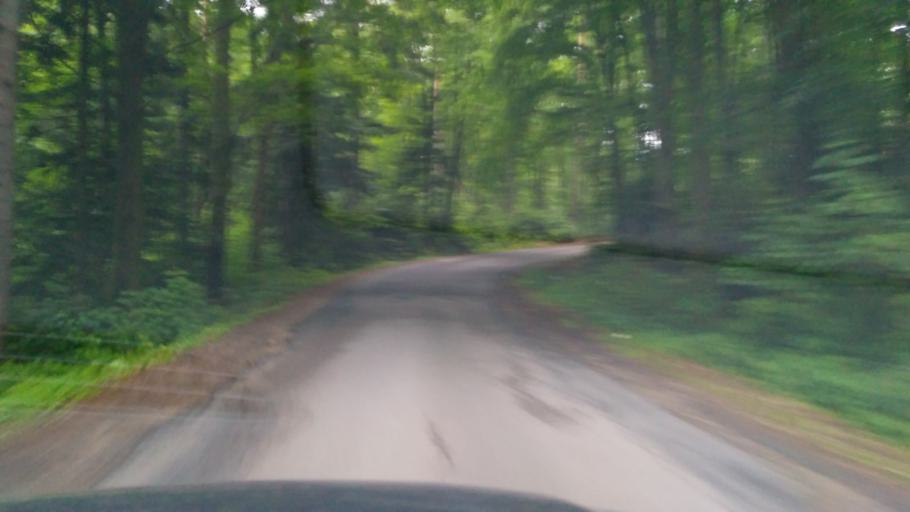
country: PL
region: Subcarpathian Voivodeship
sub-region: Powiat brzozowski
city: Jablonica Polska
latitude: 49.7240
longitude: 21.9116
